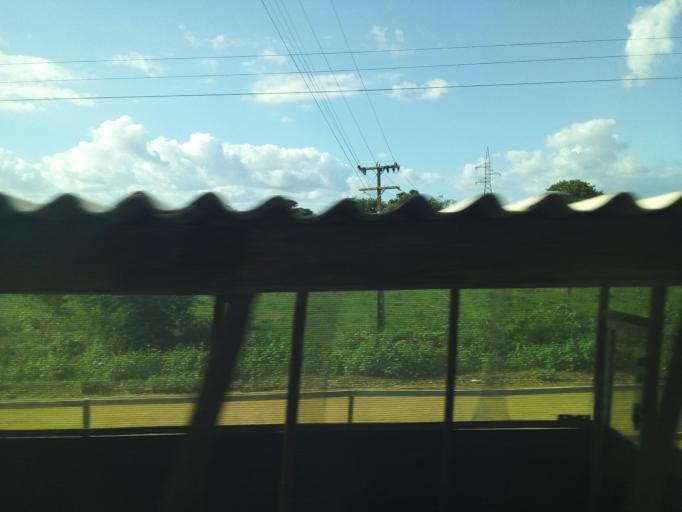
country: BR
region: Minas Gerais
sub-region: Conselheiro Pena
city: Conselheiro Pena
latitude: -19.0131
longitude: -41.5494
